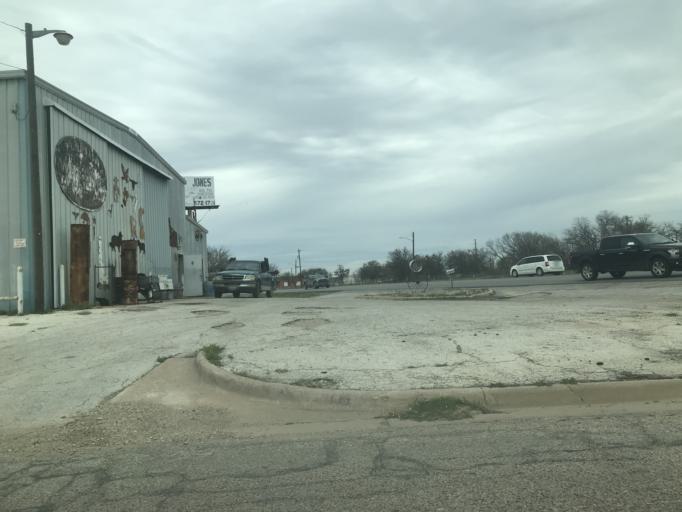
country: US
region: Texas
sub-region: Taylor County
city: Abilene
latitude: 32.4716
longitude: -99.7265
